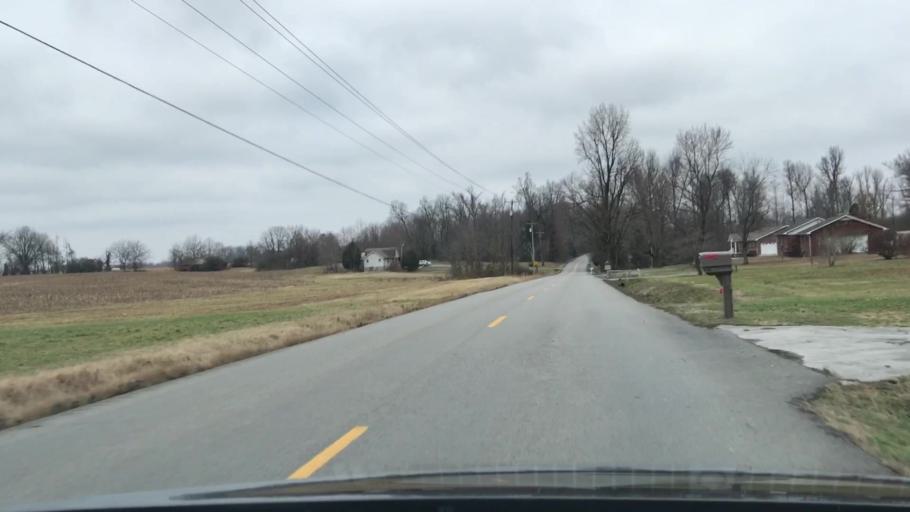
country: US
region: Kentucky
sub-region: Muhlenberg County
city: Morehead
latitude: 37.3606
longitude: -87.2327
